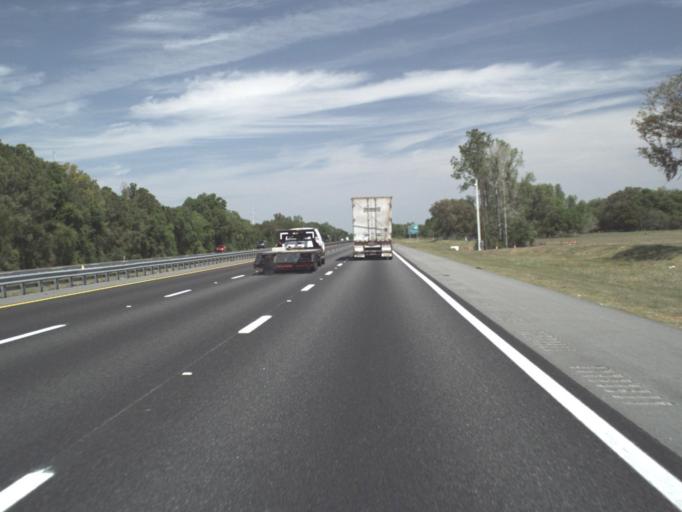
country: US
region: Florida
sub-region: Sumter County
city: Lake Panasoffkee
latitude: 28.7172
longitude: -82.1177
